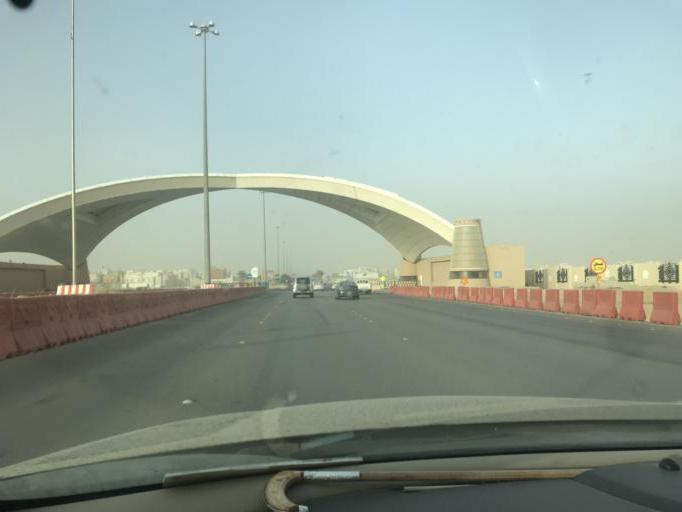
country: SA
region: Ar Riyad
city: Riyadh
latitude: 24.8555
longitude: 46.6825
